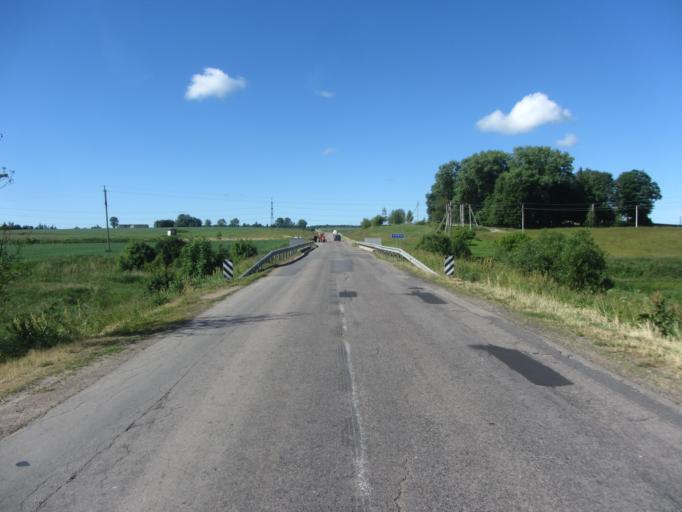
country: LT
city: Ziezmariai
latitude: 54.8012
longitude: 24.4167
